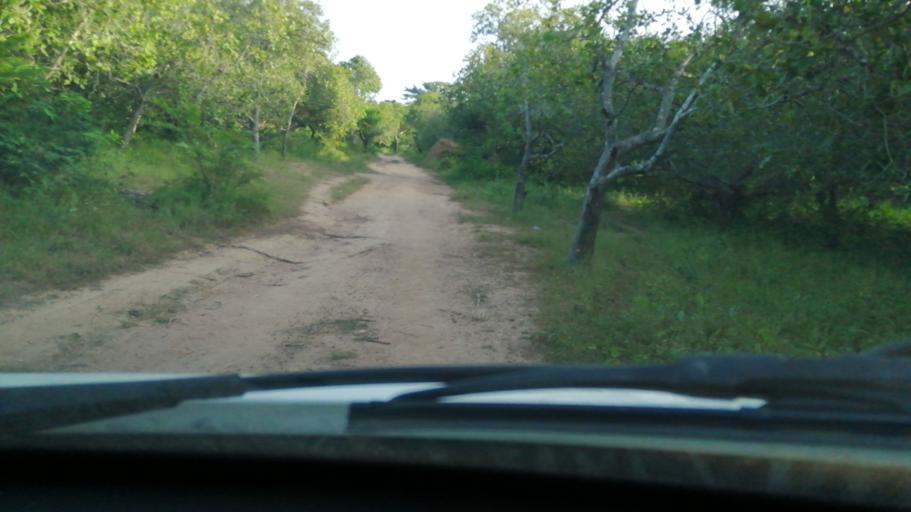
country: GW
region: Oio
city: Mansoa
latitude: 11.9984
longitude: -15.4719
